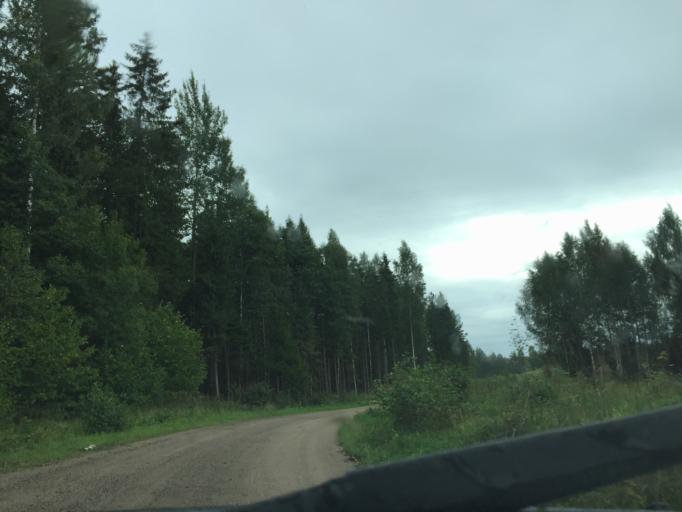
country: LV
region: Preilu Rajons
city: Jaunaglona
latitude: 56.2565
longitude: 27.1444
